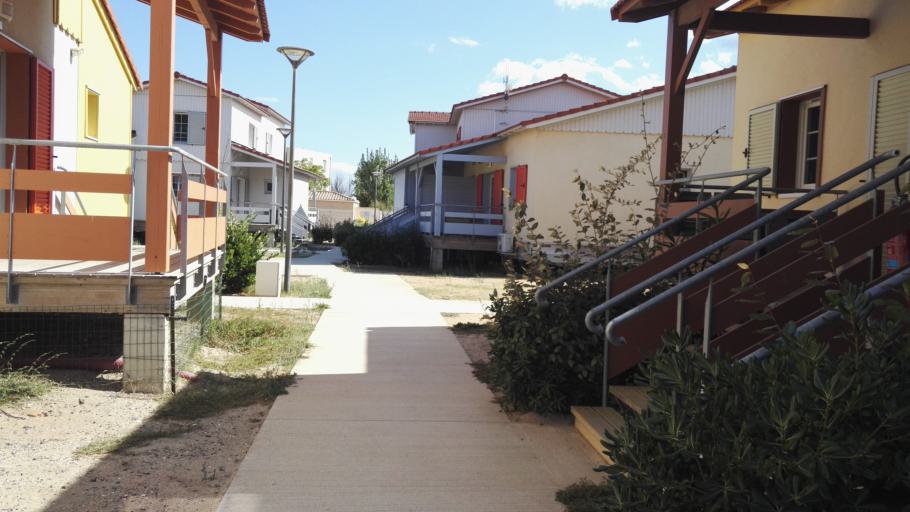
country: FR
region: Languedoc-Roussillon
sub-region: Departement de l'Herault
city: Marseillan
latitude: 43.3217
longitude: 3.5580
